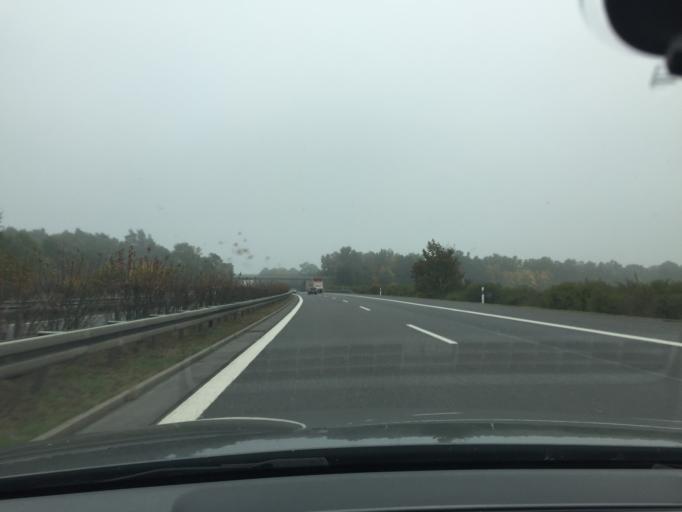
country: DE
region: Brandenburg
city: Bronkow
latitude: 51.6346
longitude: 13.9410
